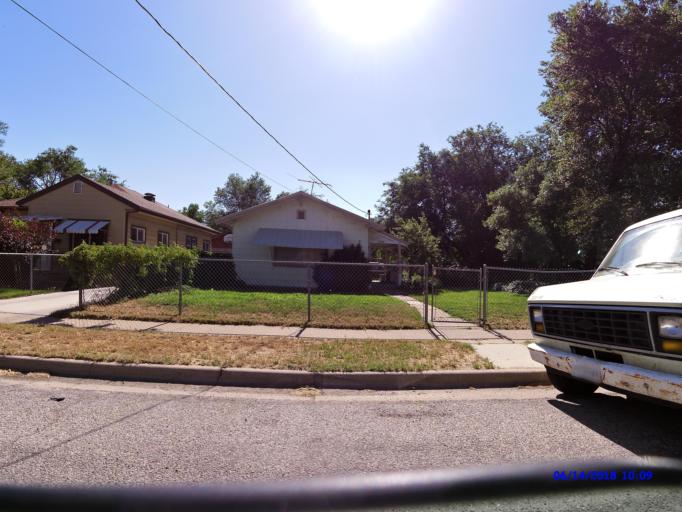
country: US
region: Utah
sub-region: Weber County
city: Ogden
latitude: 41.2239
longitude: -111.9941
